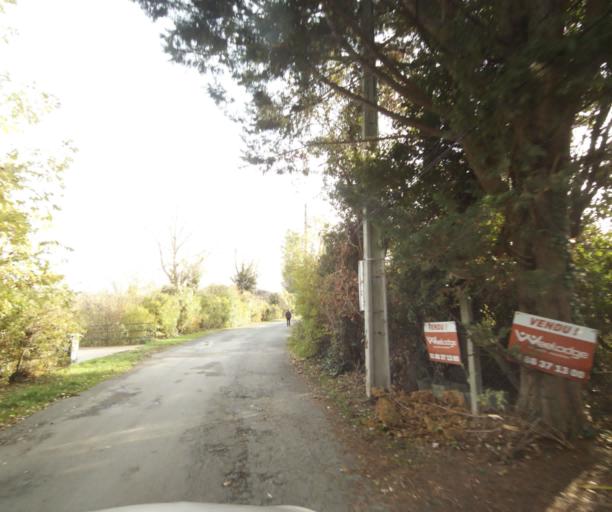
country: FR
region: Ile-de-France
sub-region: Departement du Val-d'Oise
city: Herblay
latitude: 48.9814
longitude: 2.1525
